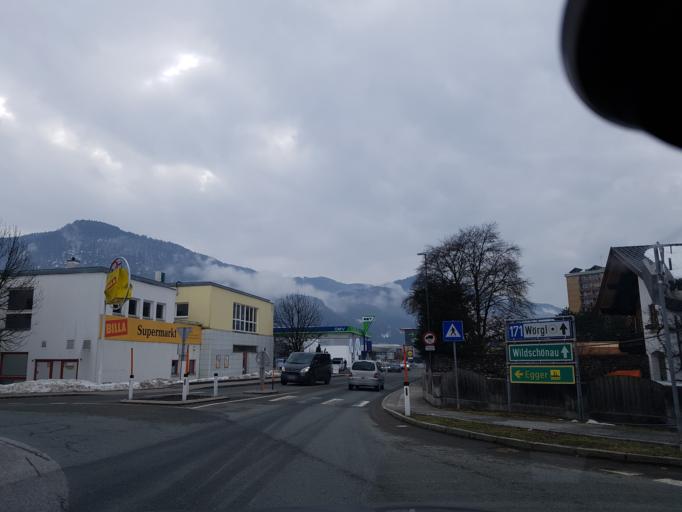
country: AT
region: Tyrol
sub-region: Politischer Bezirk Kufstein
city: Worgl
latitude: 47.4910
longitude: 12.0743
